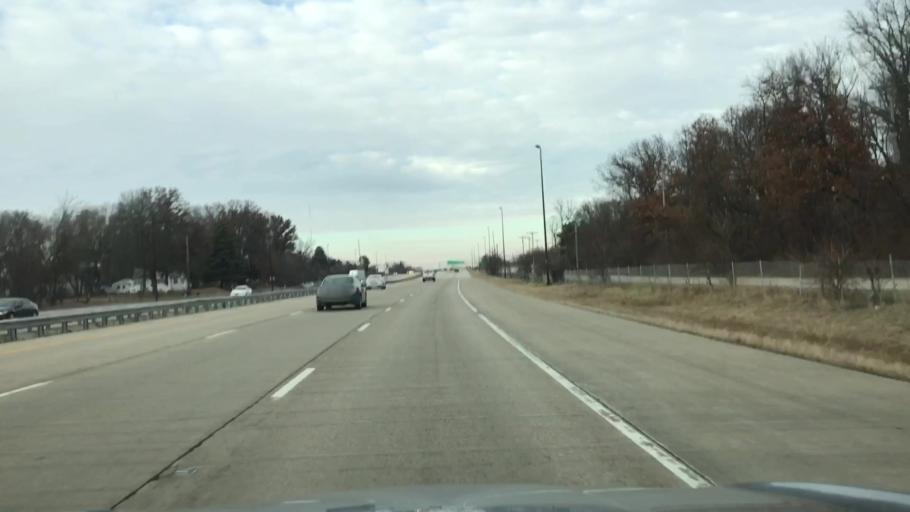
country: US
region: Illinois
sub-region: Sangamon County
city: Southern View
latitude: 39.7025
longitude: -89.6434
